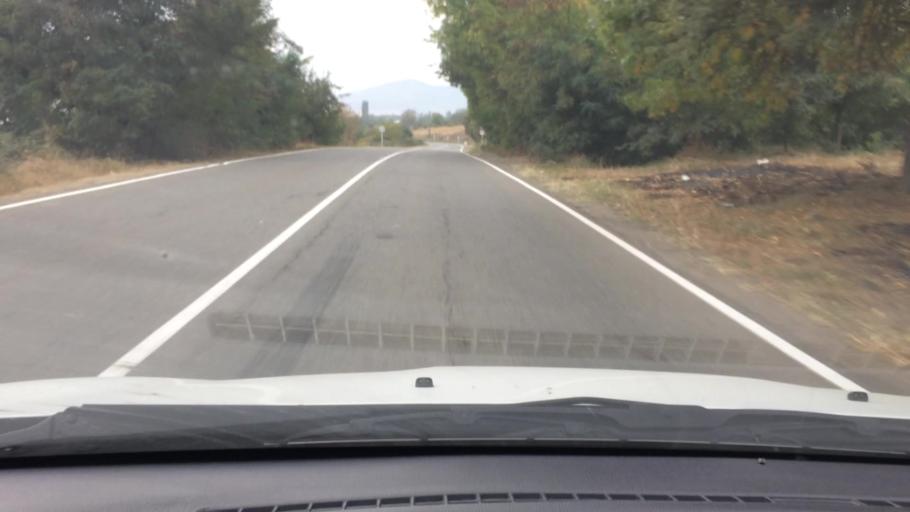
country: GE
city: Naghvarevi
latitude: 41.3183
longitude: 44.7948
